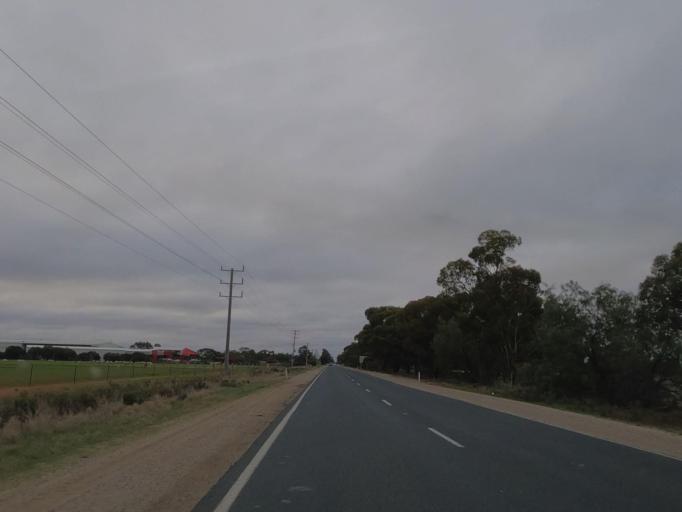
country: AU
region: Victoria
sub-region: Swan Hill
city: Swan Hill
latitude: -35.3903
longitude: 143.5697
